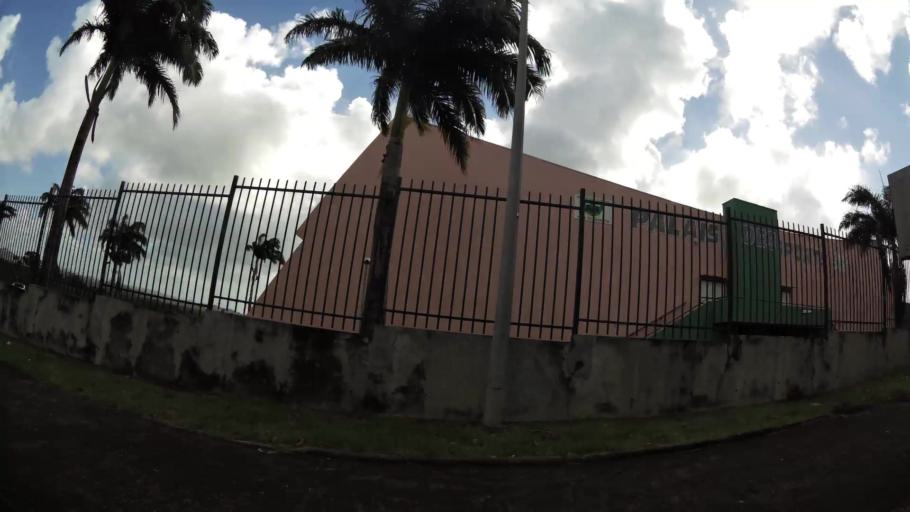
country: MQ
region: Martinique
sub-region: Martinique
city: Le Lamentin
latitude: 14.6124
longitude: -60.9961
